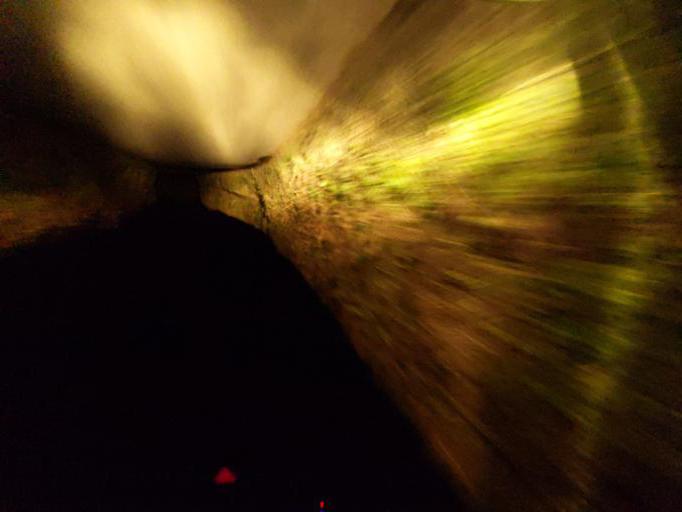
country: GB
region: England
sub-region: Cornwall
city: Torpoint
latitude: 50.3478
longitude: -4.2264
